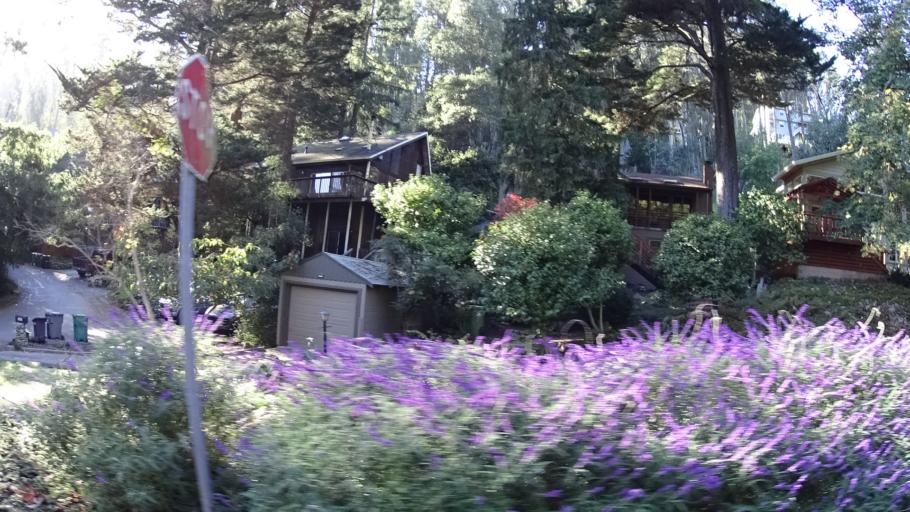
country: US
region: California
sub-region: Alameda County
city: Piedmont
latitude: 37.8459
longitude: -122.2087
